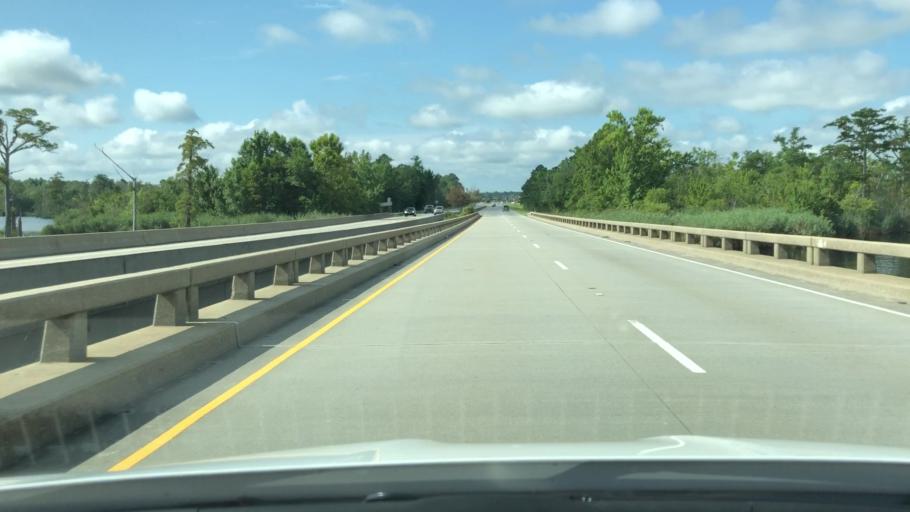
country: US
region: North Carolina
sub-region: Perquimans County
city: Hertford
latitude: 36.1869
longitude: -76.4572
